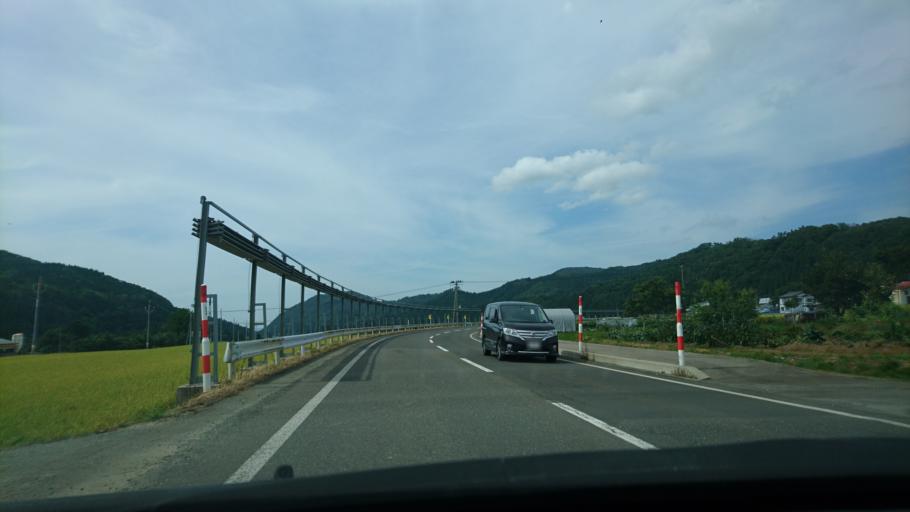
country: JP
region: Akita
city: Yuzawa
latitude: 39.1902
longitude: 140.6190
